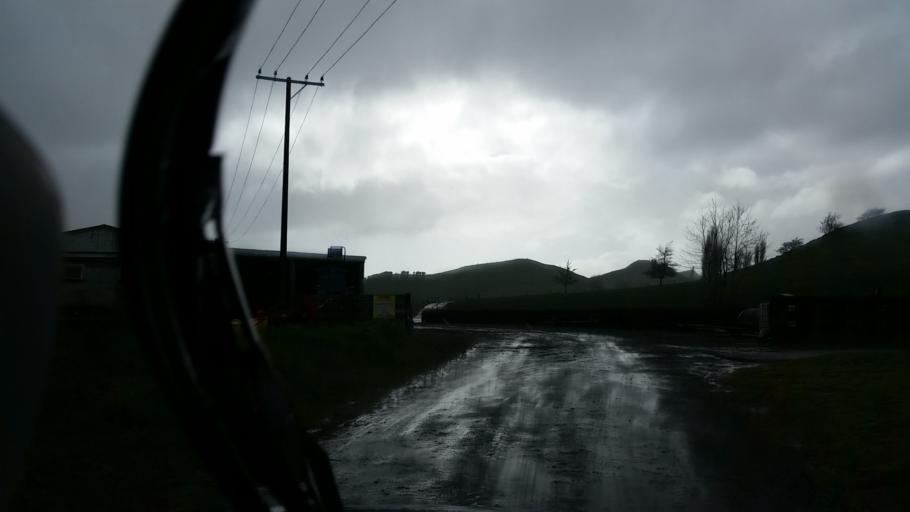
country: NZ
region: Taranaki
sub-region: South Taranaki District
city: Eltham
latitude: -39.3441
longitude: 174.4355
